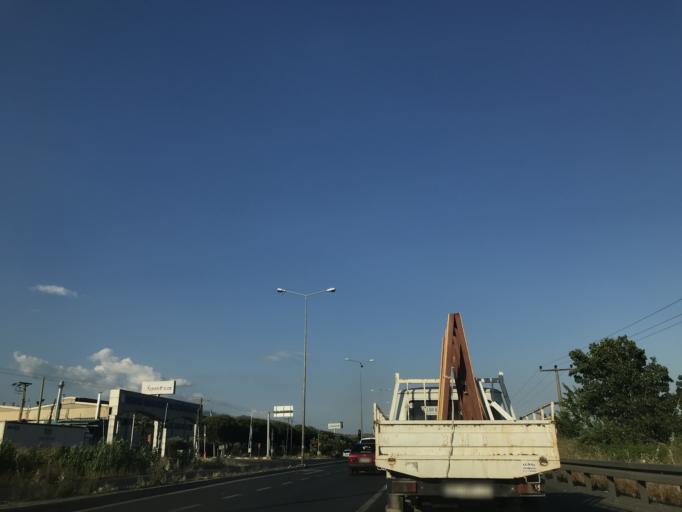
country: TR
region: Aydin
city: Umurlu
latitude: 37.8553
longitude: 27.9827
